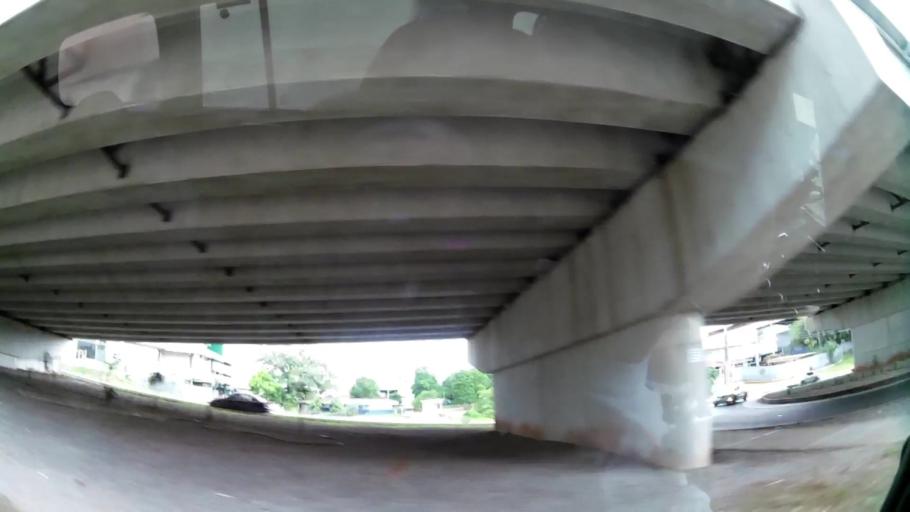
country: PA
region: Panama
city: Tocumen
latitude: 9.0639
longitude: -79.4181
